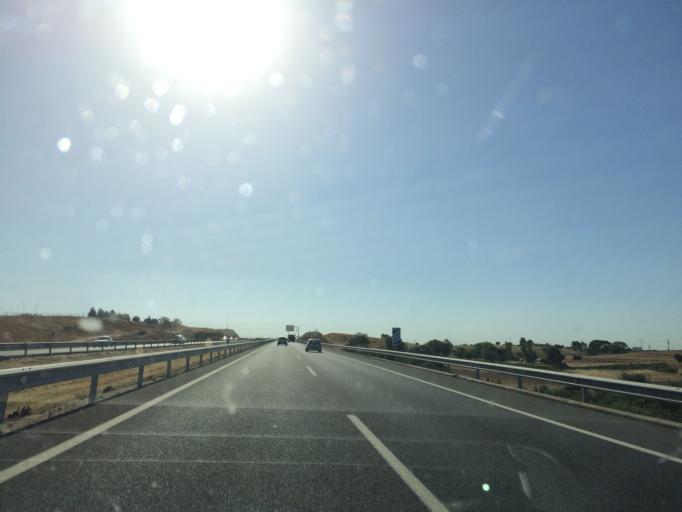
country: ES
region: Castille-La Mancha
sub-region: Province of Toledo
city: Santa Cruz del Retamar
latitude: 40.1265
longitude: -4.2336
